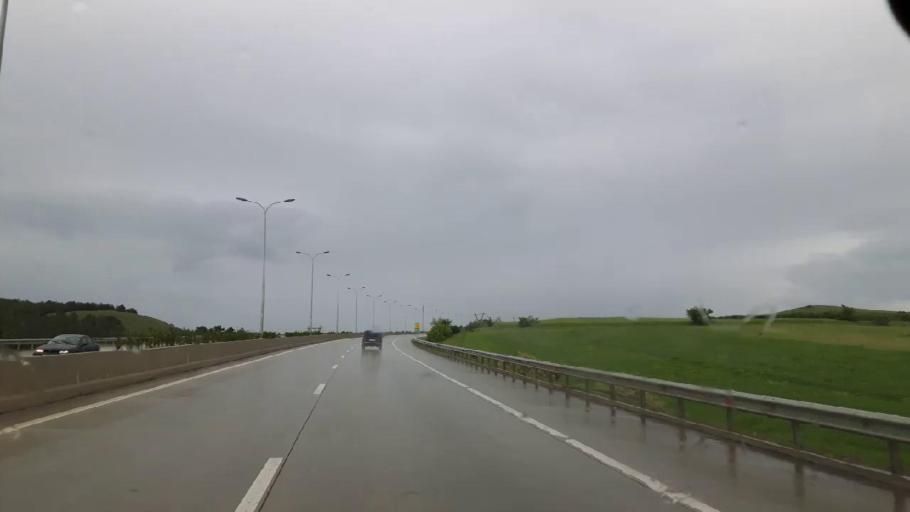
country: GE
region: Shida Kartli
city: Gori
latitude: 42.0199
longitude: 44.0086
